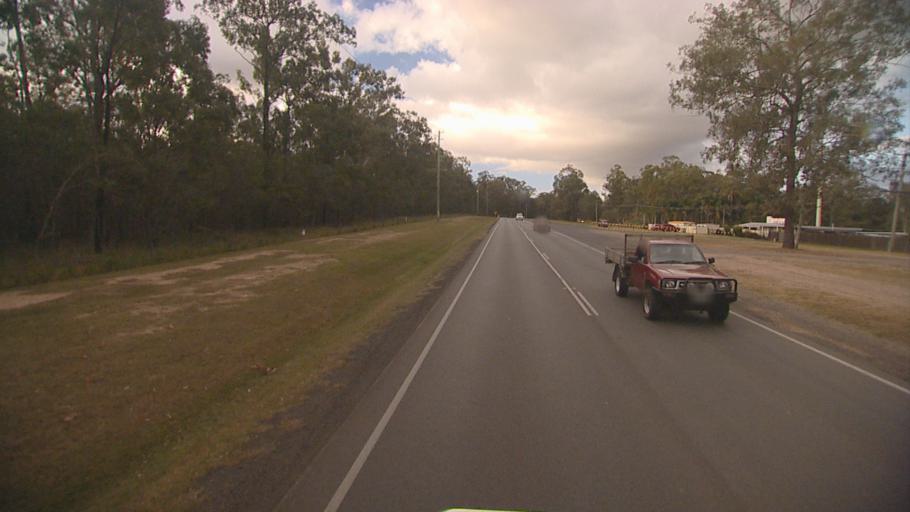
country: AU
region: Queensland
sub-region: Logan
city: Park Ridge South
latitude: -27.7102
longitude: 152.9982
